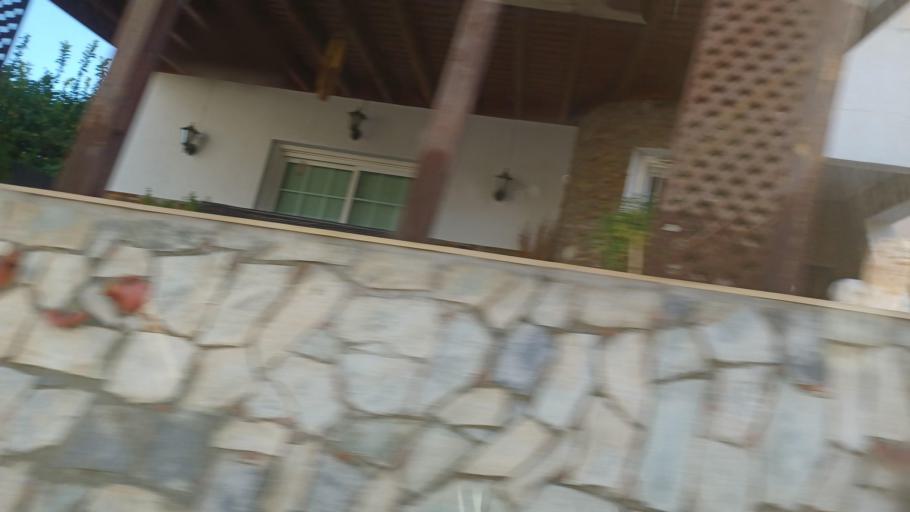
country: CY
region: Lefkosia
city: Lythrodontas
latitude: 34.9464
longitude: 33.2942
